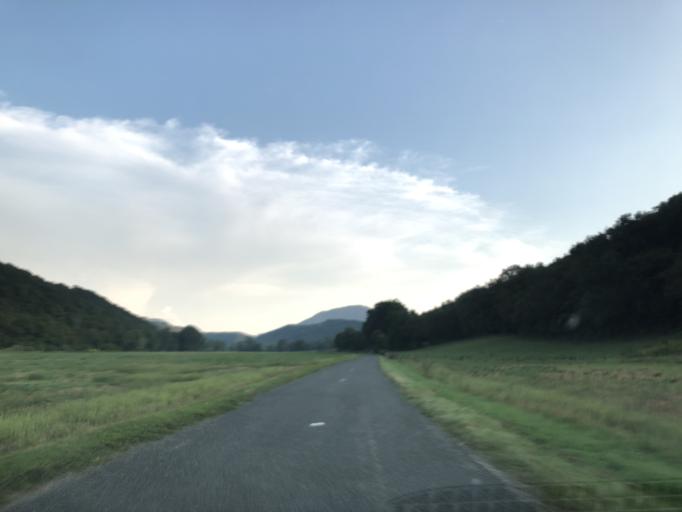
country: FR
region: Rhone-Alpes
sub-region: Departement de l'Ain
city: Belley
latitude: 45.7492
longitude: 5.6222
